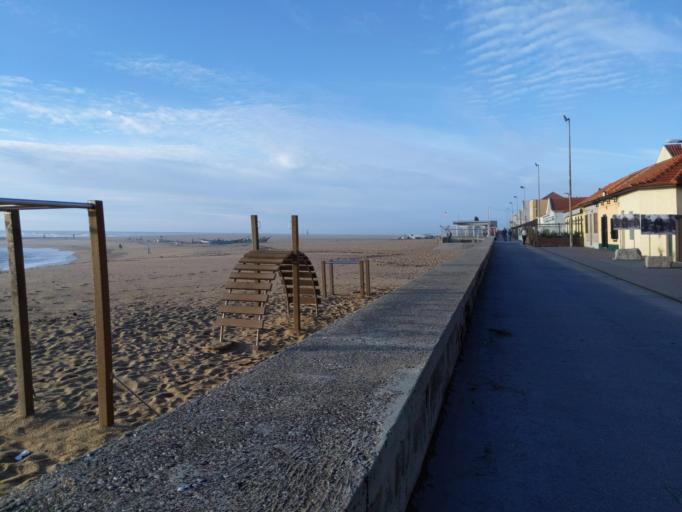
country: PT
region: Porto
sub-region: Vila Nova de Gaia
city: Arcozelo
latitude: 41.0480
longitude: -8.6536
